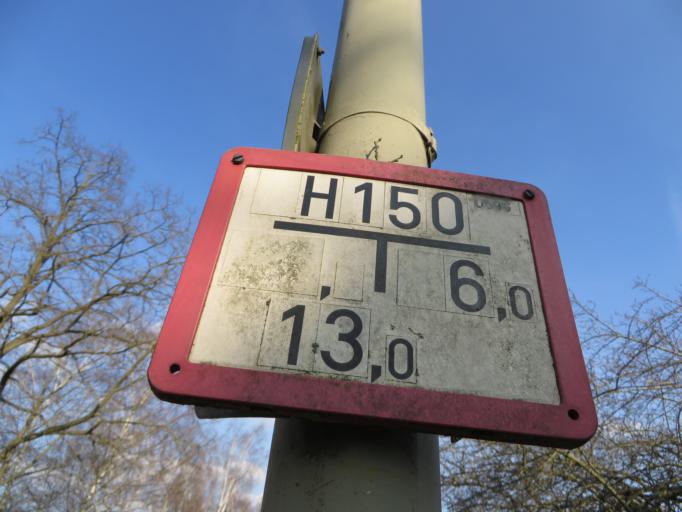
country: DE
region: North Rhine-Westphalia
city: Witten
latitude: 51.4500
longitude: 7.3495
